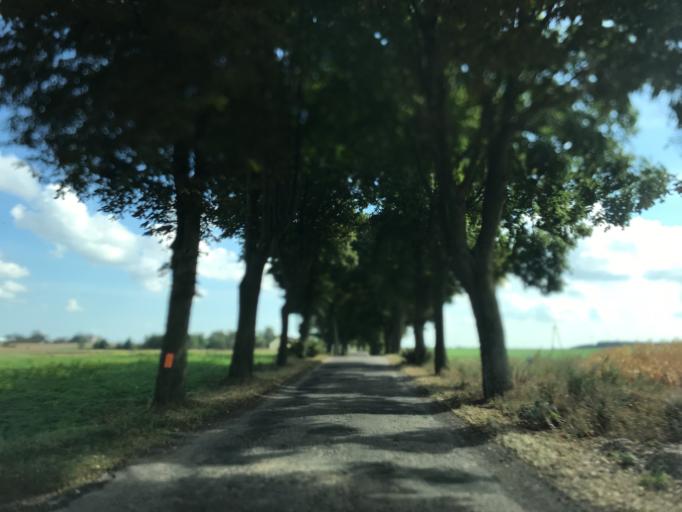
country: PL
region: Kujawsko-Pomorskie
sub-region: Powiat brodnicki
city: Brzozie
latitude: 53.3509
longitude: 19.6454
